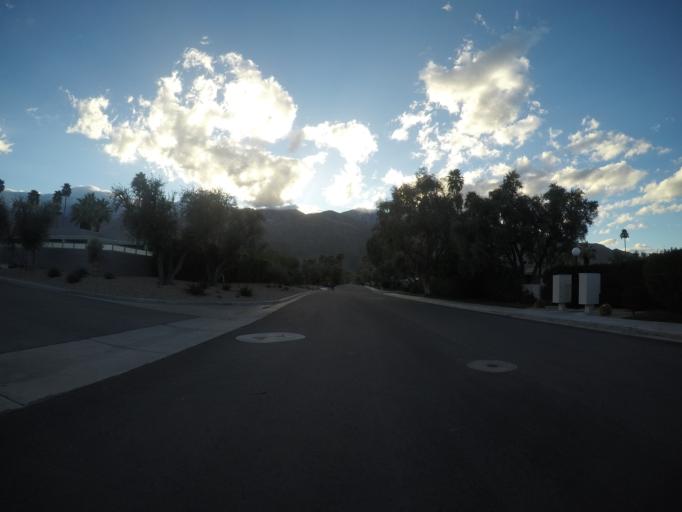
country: US
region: California
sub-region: Riverside County
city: Palm Springs
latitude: 33.7981
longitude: -116.5330
